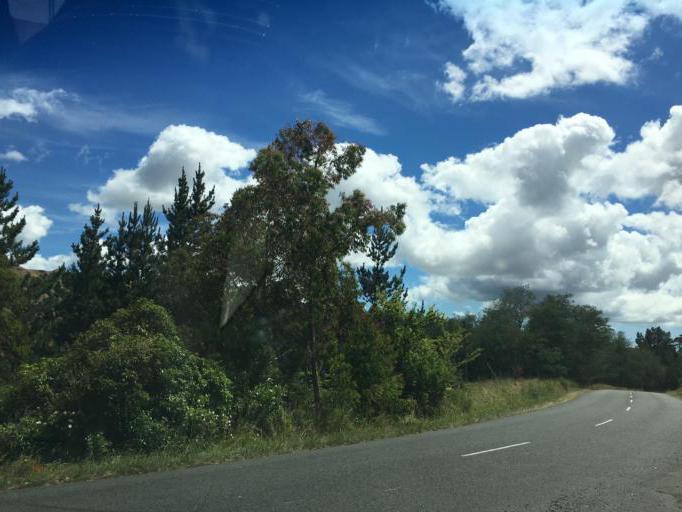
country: NZ
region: Hawke's Bay
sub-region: Hastings District
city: Hastings
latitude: -39.7565
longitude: 176.8642
